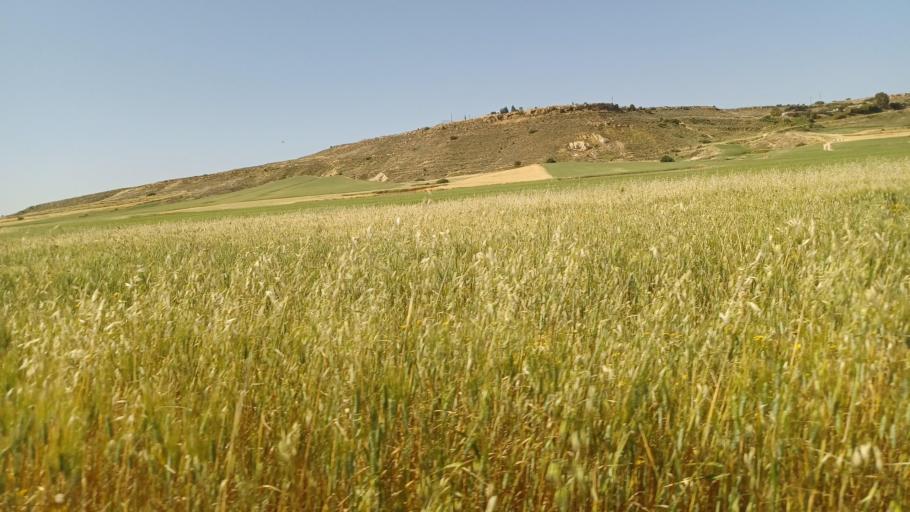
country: CY
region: Lefkosia
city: Mammari
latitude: 35.1692
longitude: 33.2359
